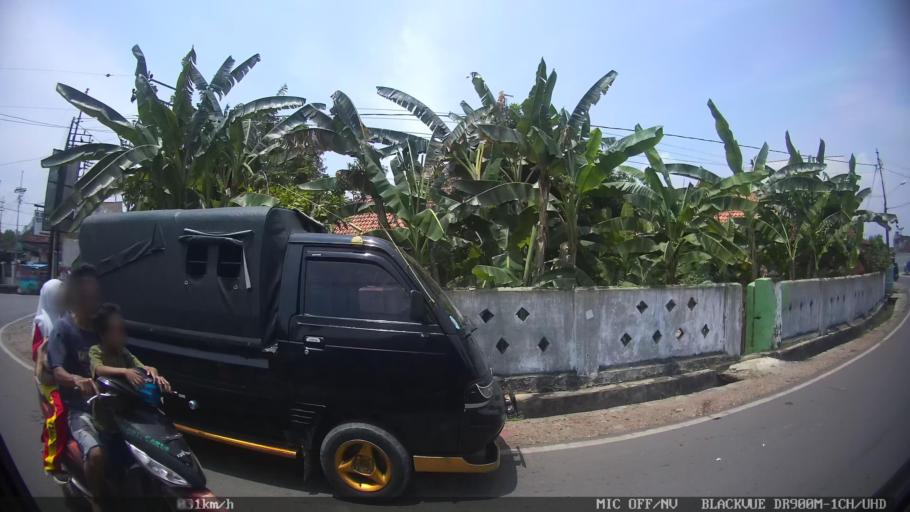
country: ID
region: Lampung
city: Bandarlampung
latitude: -5.4502
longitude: 105.2569
